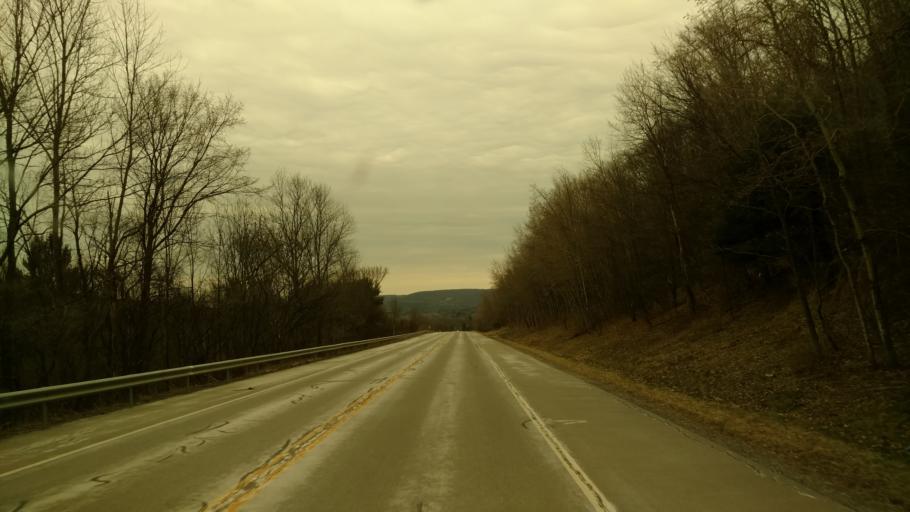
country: US
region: New York
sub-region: Allegany County
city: Wellsville
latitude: 42.0713
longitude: -77.9191
